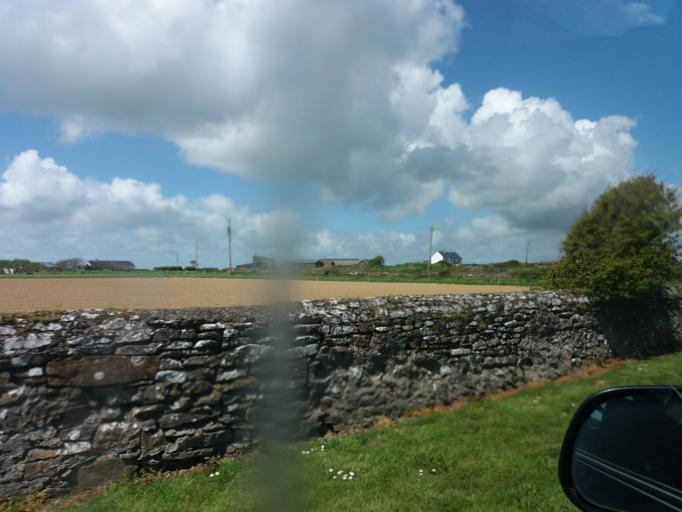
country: IE
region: Munster
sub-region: Waterford
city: Dunmore East
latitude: 52.1540
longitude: -6.8983
